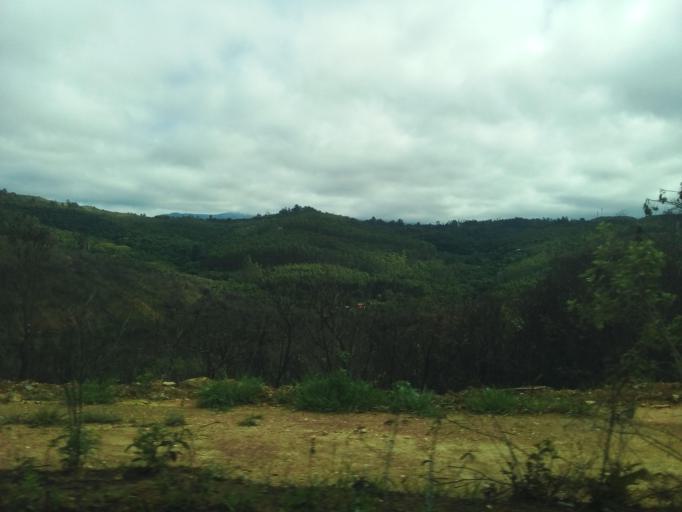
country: BR
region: Minas Gerais
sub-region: Caete
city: Caete
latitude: -19.9079
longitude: -43.6951
